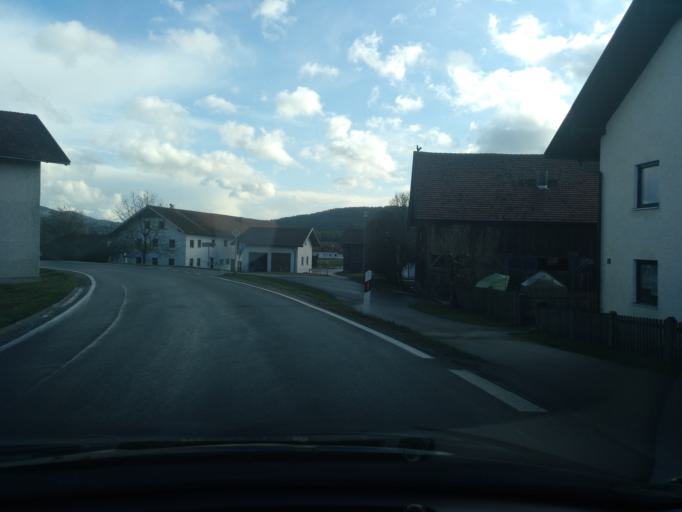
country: DE
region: Bavaria
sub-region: Lower Bavaria
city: Konzell
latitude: 49.1032
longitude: 12.7197
